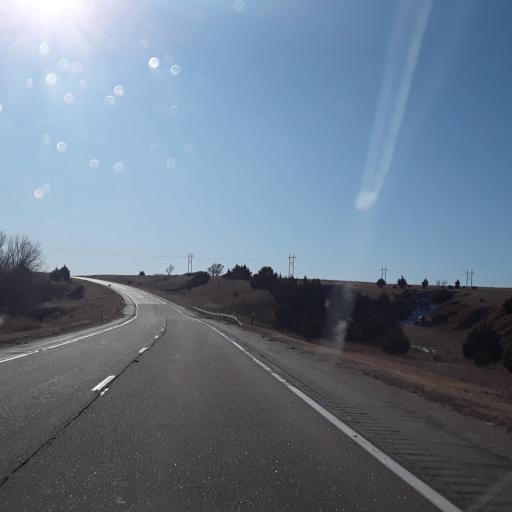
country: US
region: Nebraska
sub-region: Frontier County
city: Stockville
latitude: 40.5434
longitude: -100.6455
